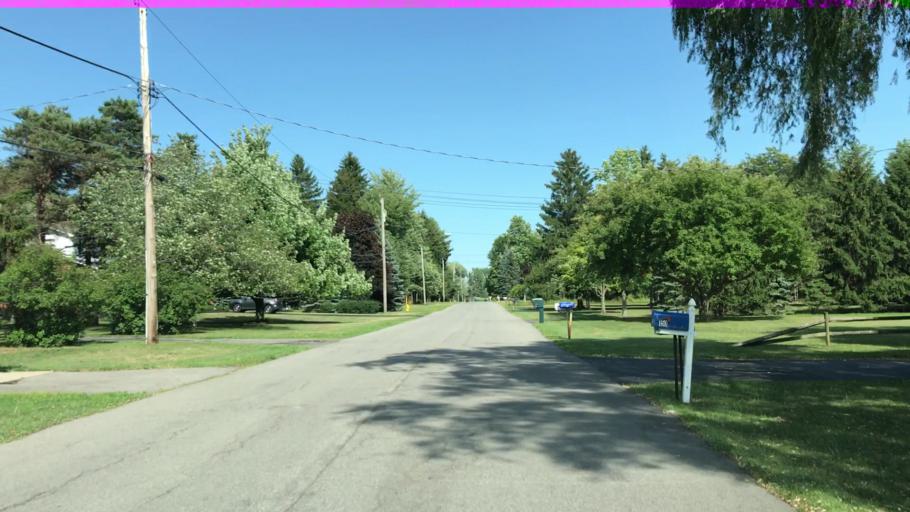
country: US
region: New York
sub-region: Erie County
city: Depew
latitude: 42.8850
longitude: -78.7041
